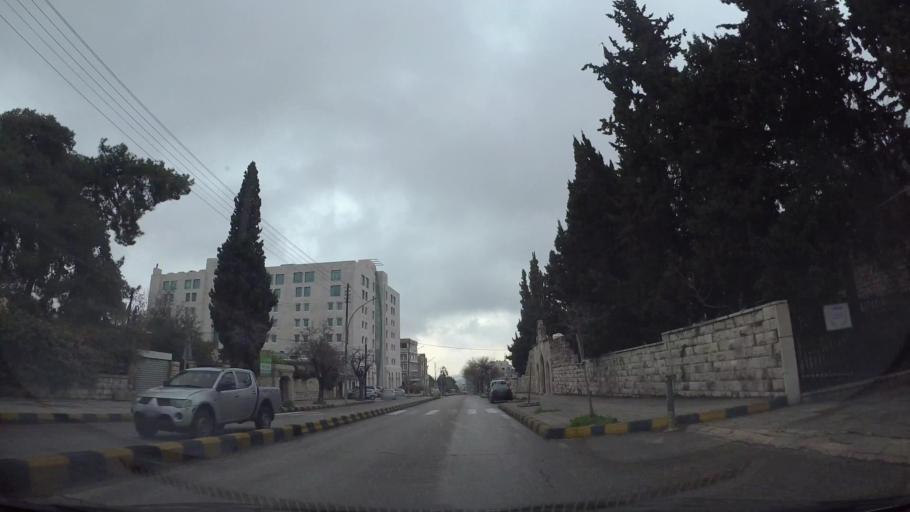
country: JO
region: Amman
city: Amman
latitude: 31.9507
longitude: 35.9182
